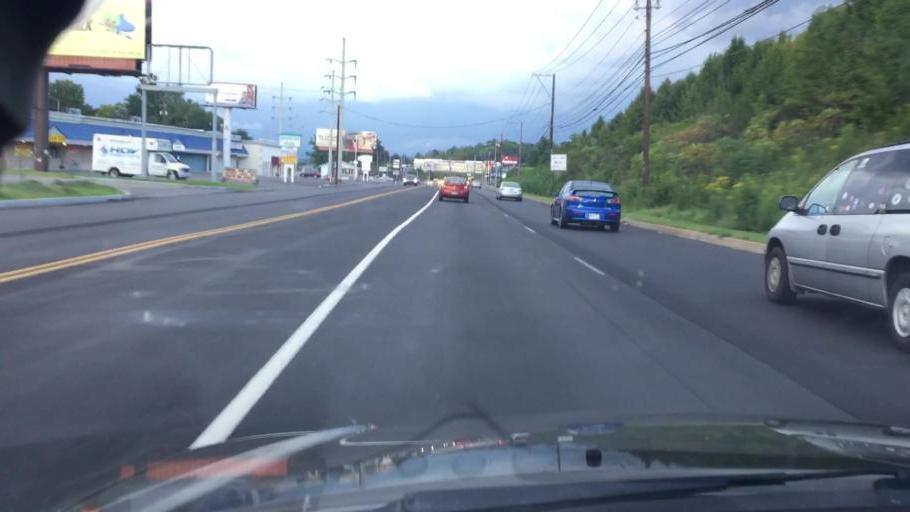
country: US
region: Pennsylvania
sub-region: Luzerne County
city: Georgetown
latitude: 41.2363
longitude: -75.8636
